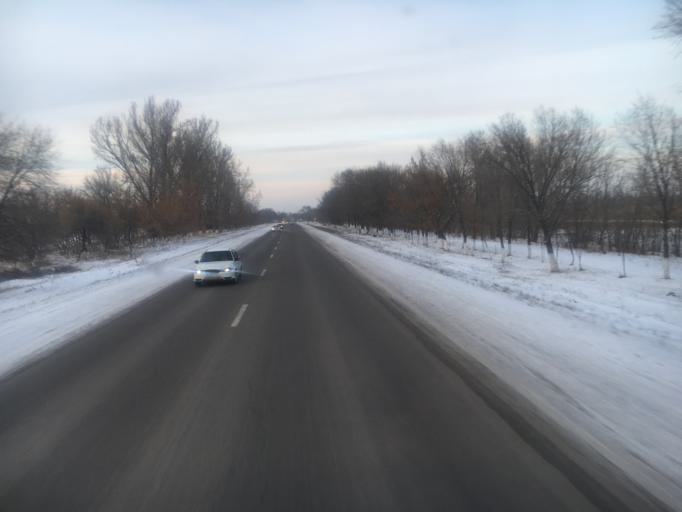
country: KZ
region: Almaty Oblysy
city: Burunday
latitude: 43.3603
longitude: 76.6439
